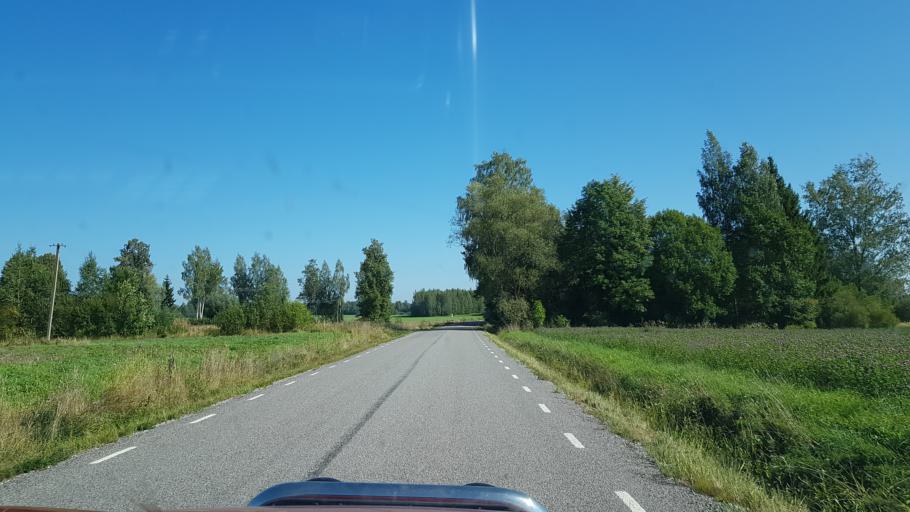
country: EE
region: Polvamaa
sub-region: Polva linn
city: Polva
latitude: 58.2155
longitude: 27.1879
